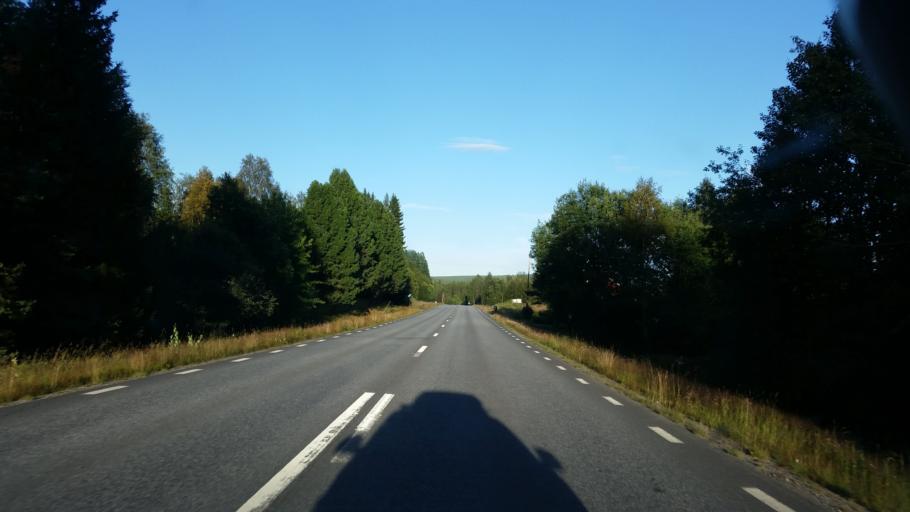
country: SE
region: Vaesterbotten
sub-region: Dorotea Kommun
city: Dorotea
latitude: 64.2553
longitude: 16.4522
